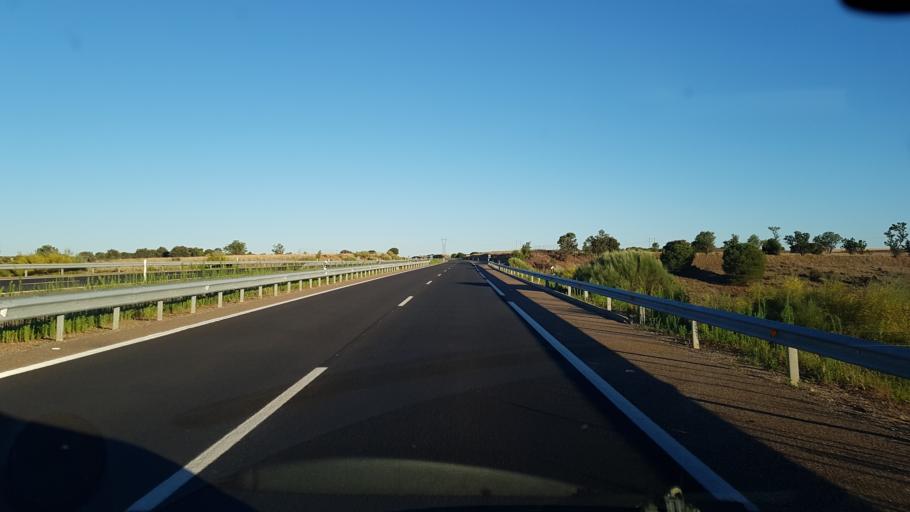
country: ES
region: Castille and Leon
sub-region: Provincia de Zamora
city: Toro
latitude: 41.5442
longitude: -5.4192
